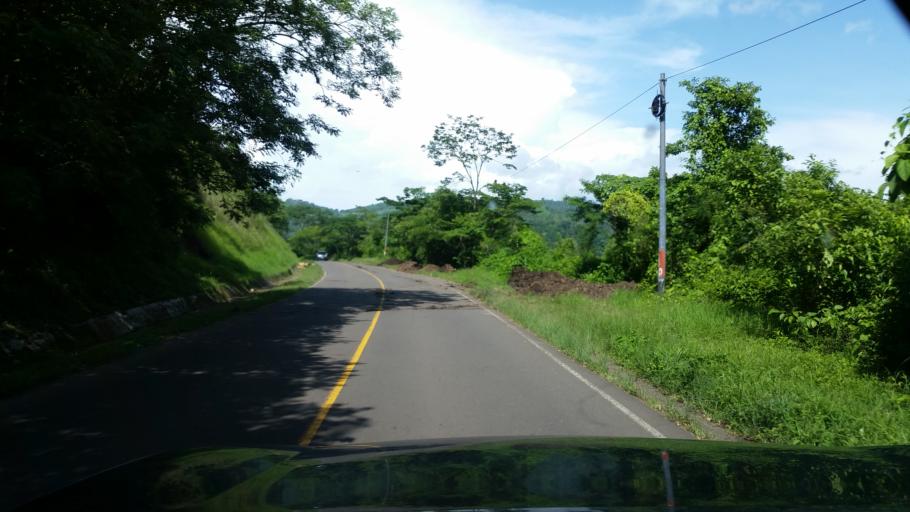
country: NI
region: Matagalpa
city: San Ramon
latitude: 13.0139
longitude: -85.7912
